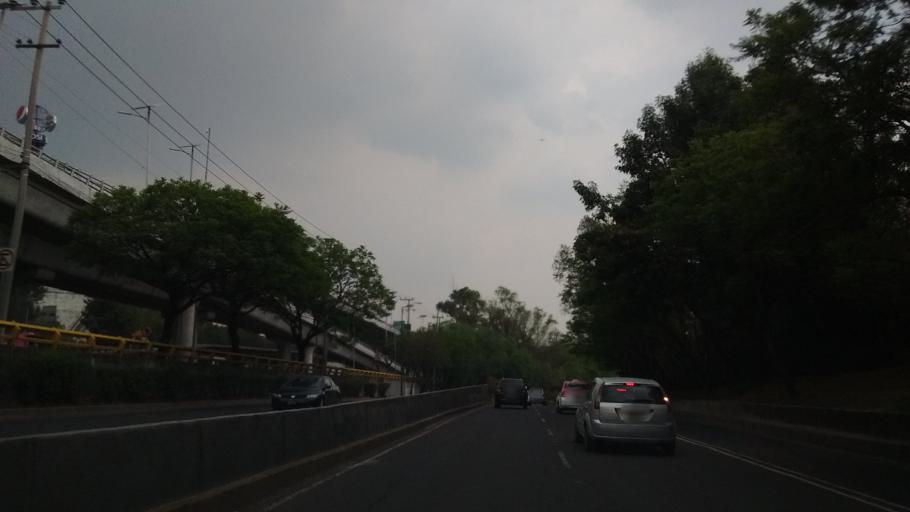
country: MX
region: Mexico City
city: Polanco
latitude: 19.4158
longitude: -99.1935
